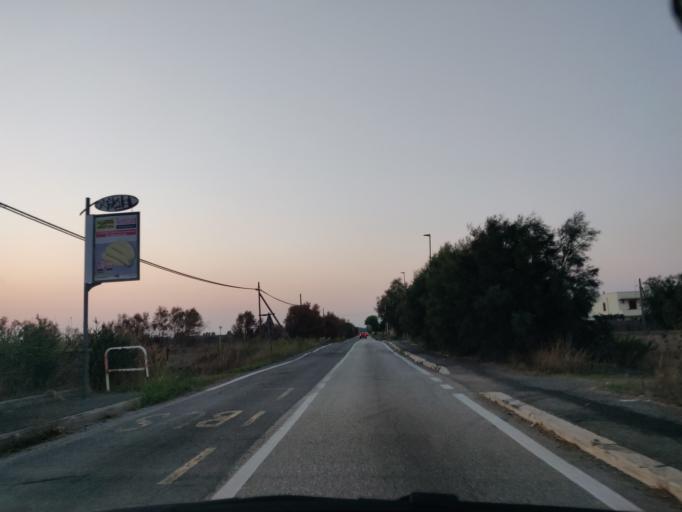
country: IT
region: Latium
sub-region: Citta metropolitana di Roma Capitale
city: Npp 23 (Parco Leonardo)
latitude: 41.8157
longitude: 12.2991
